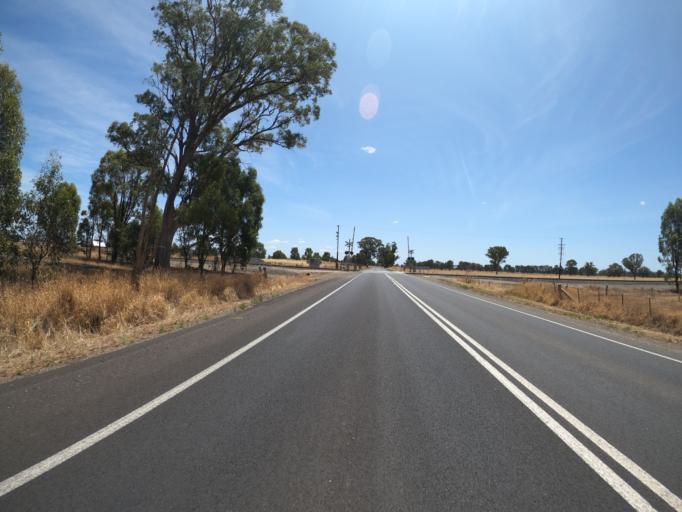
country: AU
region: Victoria
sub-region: Benalla
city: Benalla
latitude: -36.5236
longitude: 146.0369
